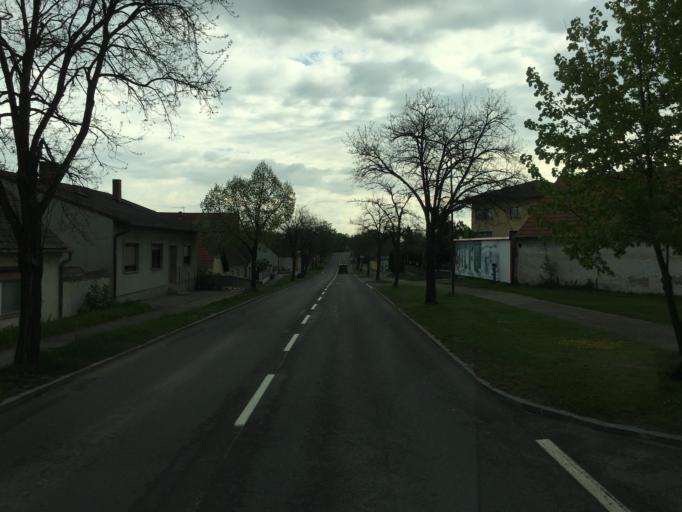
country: AT
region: Burgenland
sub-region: Politischer Bezirk Neusiedl am See
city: Potzneusiedl
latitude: 48.0150
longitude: 16.9258
